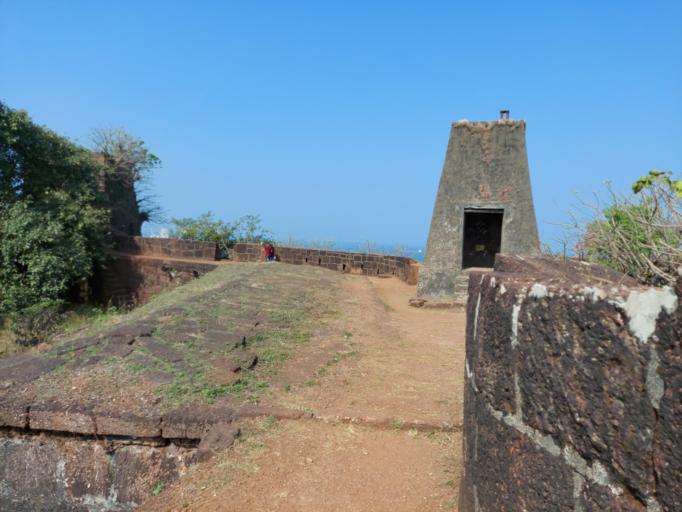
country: IN
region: Maharashtra
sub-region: Ratnagiri
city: Guhagar
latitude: 17.3017
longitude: 73.2214
